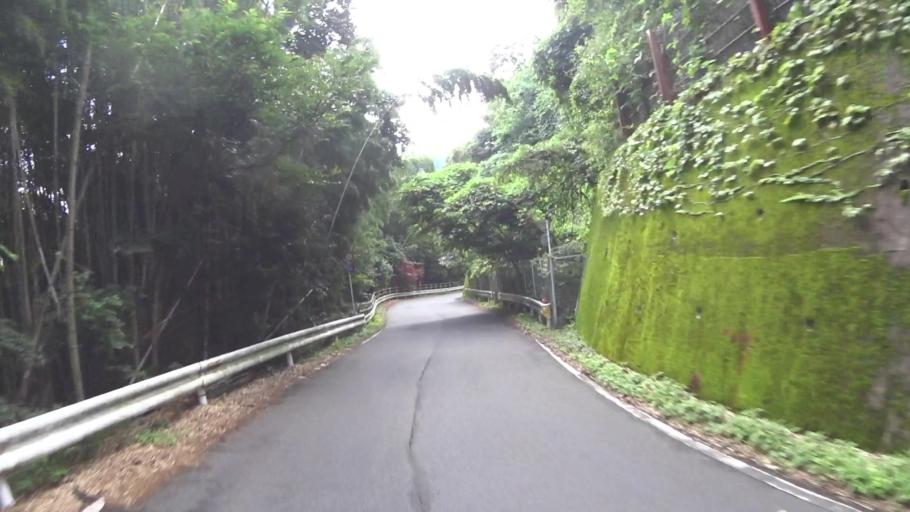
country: JP
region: Kyoto
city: Kyoto
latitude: 34.9772
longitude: 135.7904
